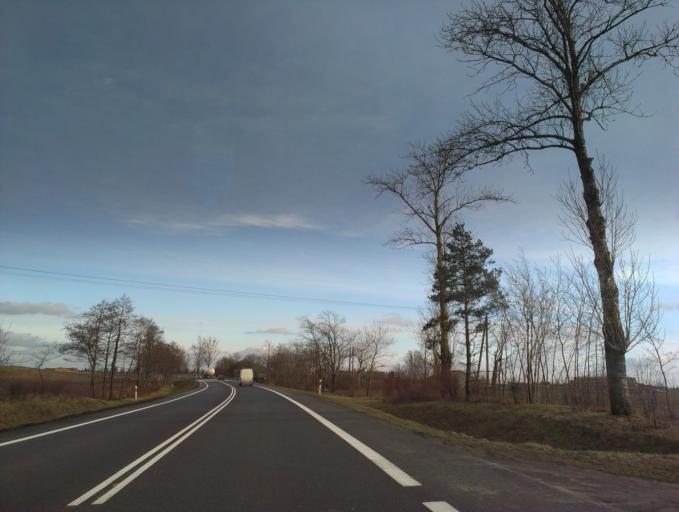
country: PL
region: Kujawsko-Pomorskie
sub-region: Powiat torunski
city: Czernikowo
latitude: 52.9310
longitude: 19.0283
